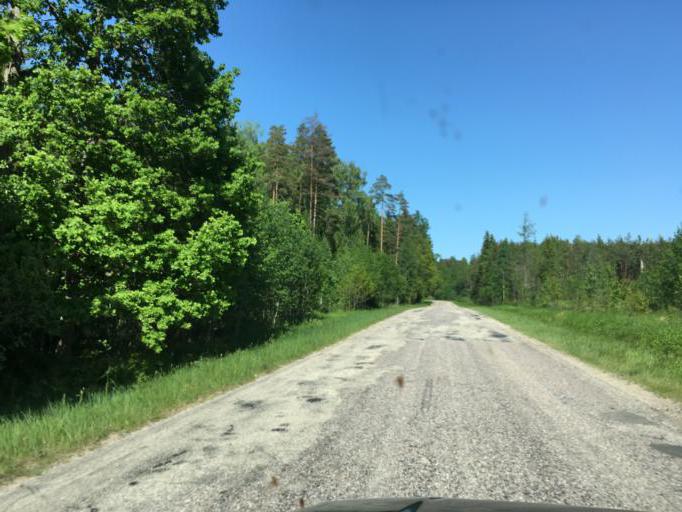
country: LV
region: Dundaga
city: Dundaga
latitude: 57.4805
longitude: 22.3345
